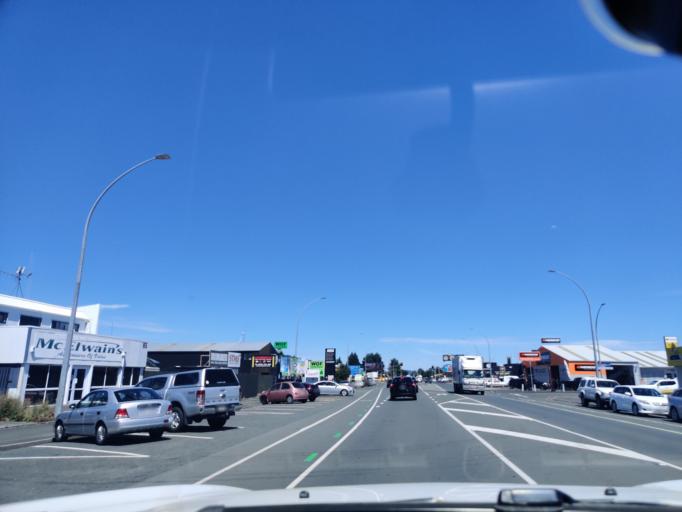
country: NZ
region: Waikato
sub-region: Hamilton City
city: Hamilton
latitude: -37.7949
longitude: 175.2631
